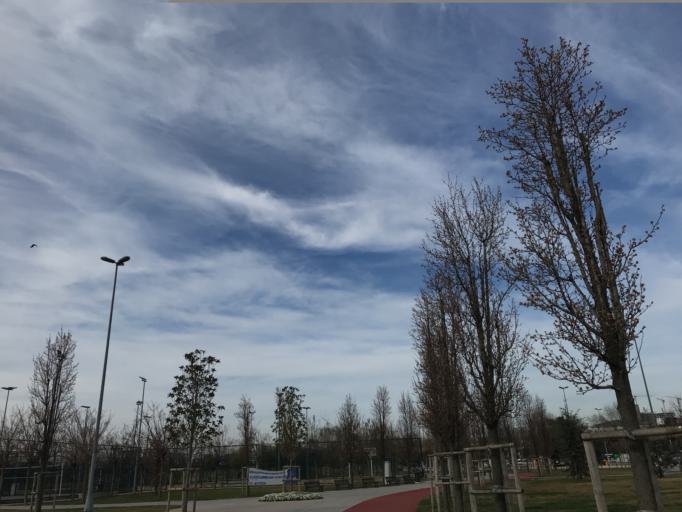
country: TR
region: Istanbul
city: Maltepe
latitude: 40.9360
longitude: 29.1127
